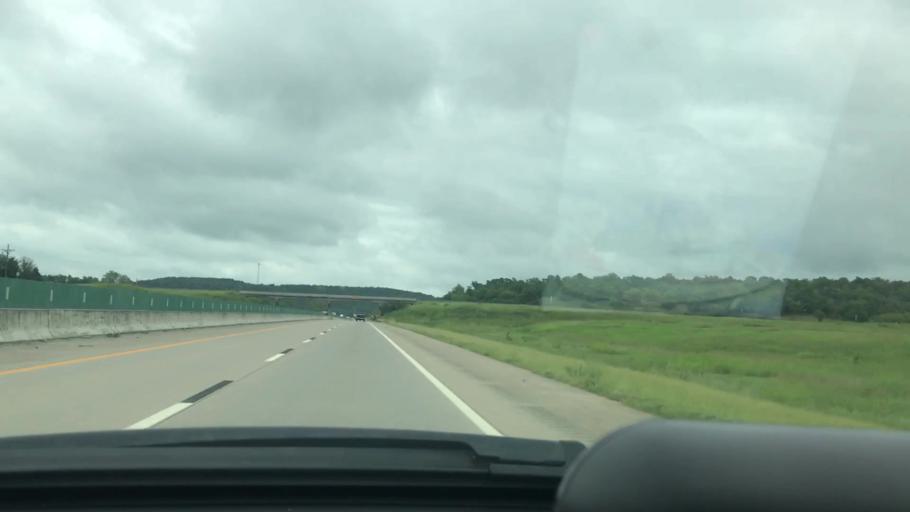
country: US
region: Oklahoma
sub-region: Pittsburg County
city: Krebs
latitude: 35.0995
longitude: -95.6973
